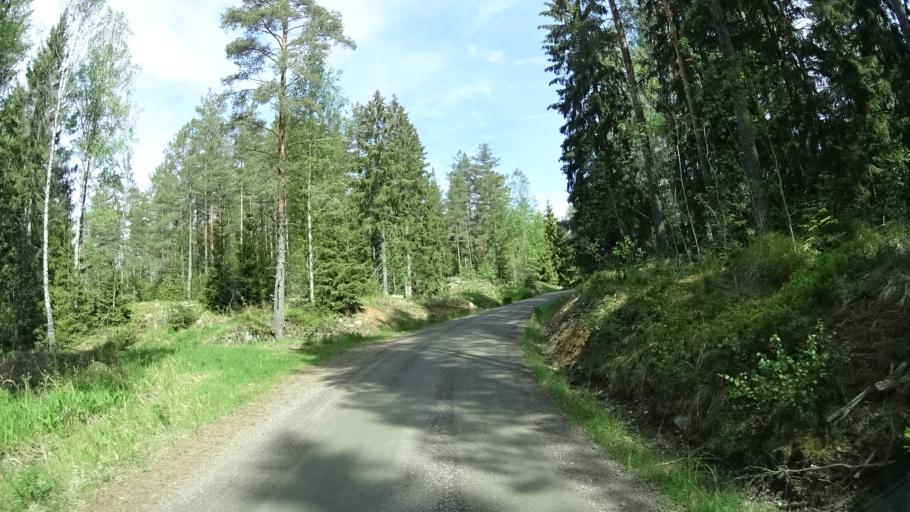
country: SE
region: OEstergoetland
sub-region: Finspangs Kommun
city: Finspang
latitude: 58.7673
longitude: 15.8465
